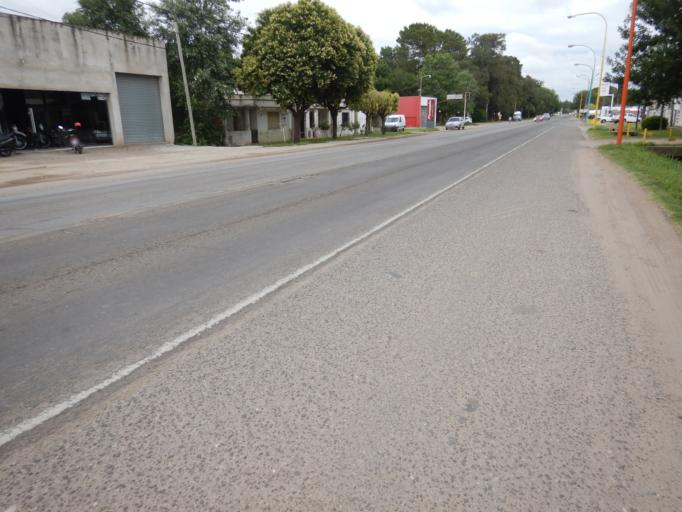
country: AR
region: Santa Fe
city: Canada de Gomez
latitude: -32.8085
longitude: -61.4043
